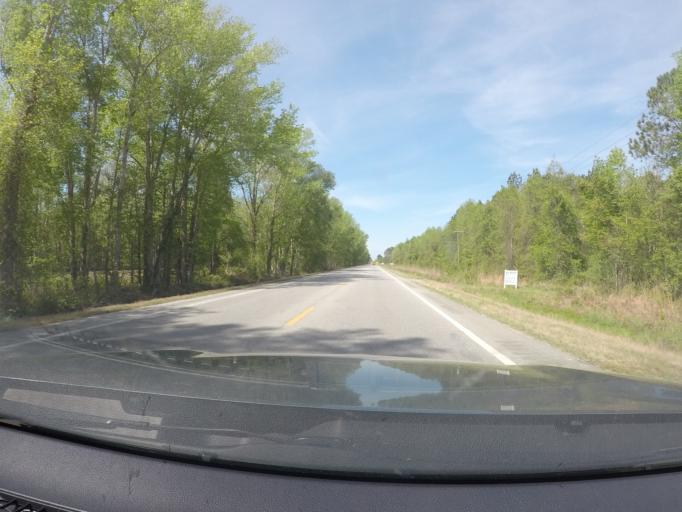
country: US
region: Georgia
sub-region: Bryan County
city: Pembroke
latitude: 32.1342
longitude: -81.6002
